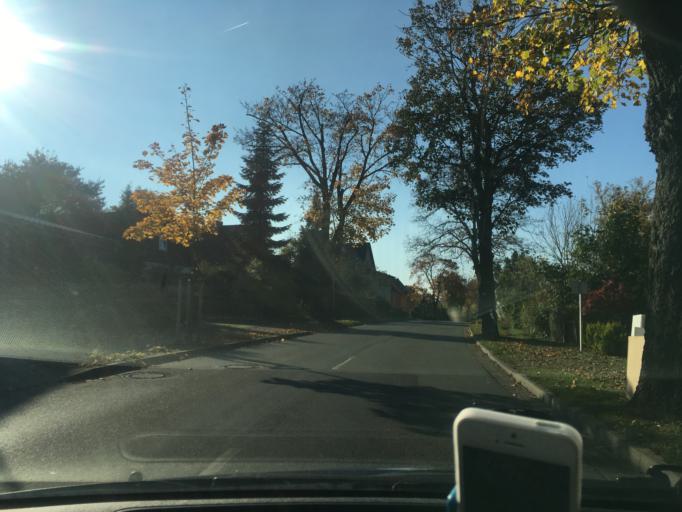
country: DE
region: Mecklenburg-Vorpommern
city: Stralendorf
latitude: 53.5731
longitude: 11.2972
